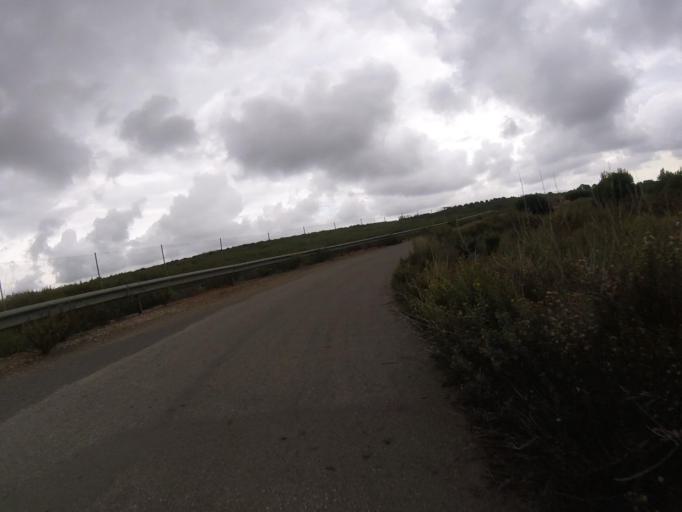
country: ES
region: Valencia
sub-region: Provincia de Castello
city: Benlloch
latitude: 40.2176
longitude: 0.0866
